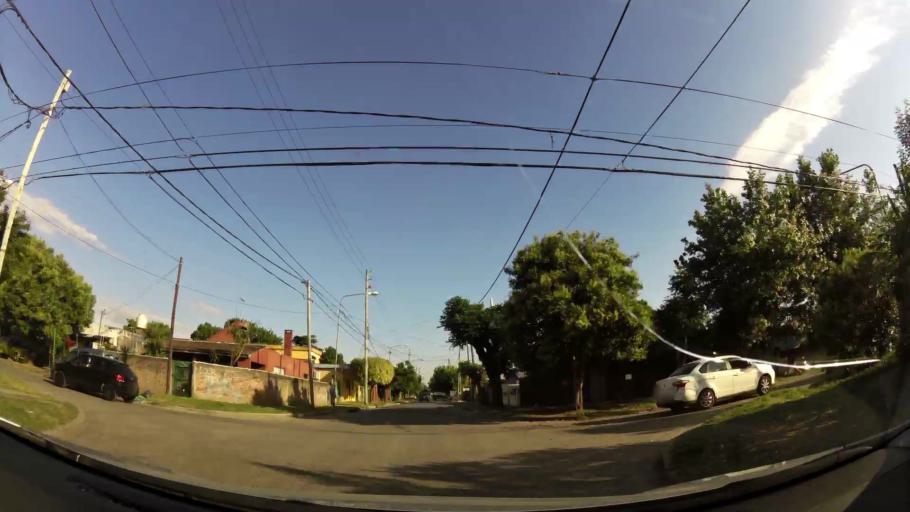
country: AR
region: Buenos Aires
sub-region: Partido de Tigre
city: Tigre
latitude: -34.4662
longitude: -58.6630
